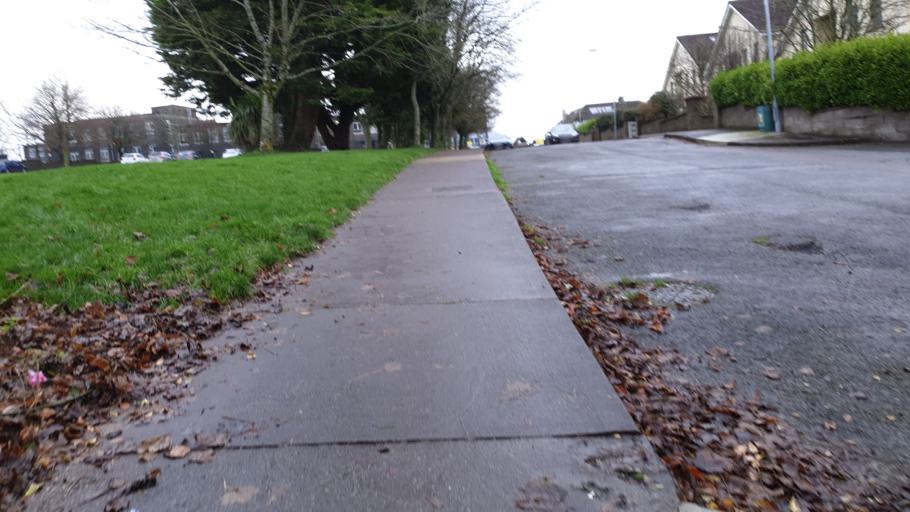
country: IE
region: Munster
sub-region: County Cork
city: Cork
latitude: 51.8880
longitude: -8.4284
